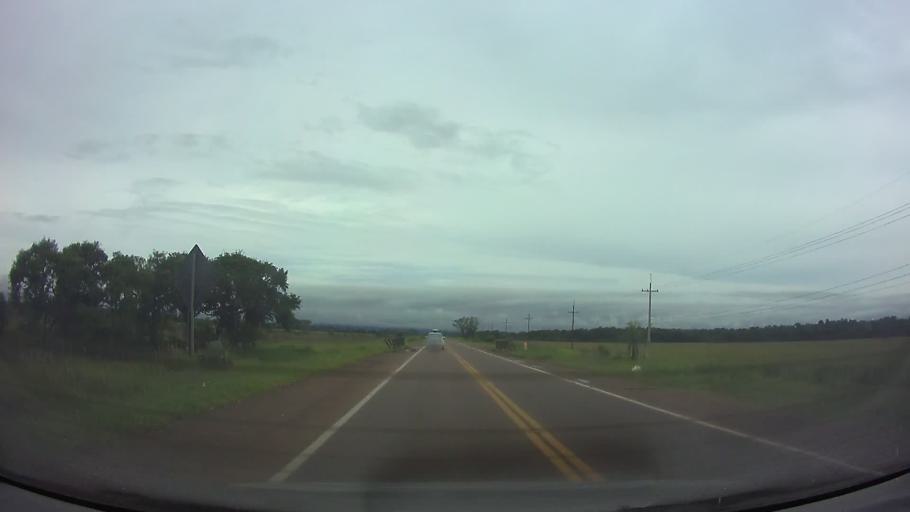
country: PY
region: Paraguari
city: Carapegua
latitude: -25.7222
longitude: -57.2028
